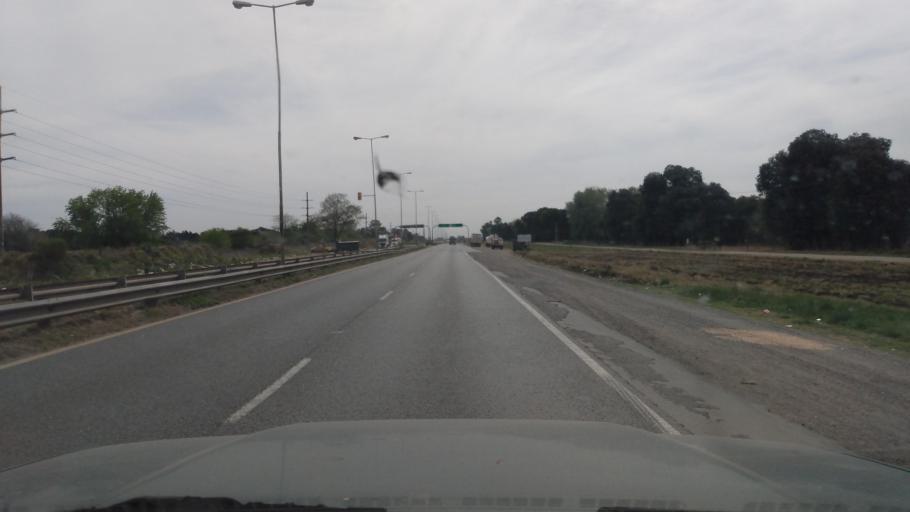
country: AR
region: Buenos Aires
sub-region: Partido de Lujan
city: Lujan
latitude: -34.5689
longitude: -59.0369
